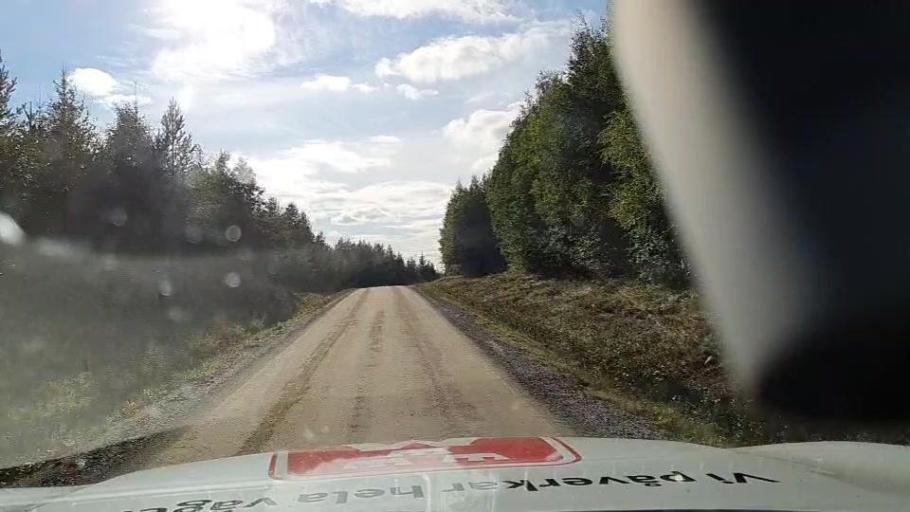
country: SE
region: Jaemtland
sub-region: Stroemsunds Kommun
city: Stroemsund
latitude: 63.7210
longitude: 16.0723
